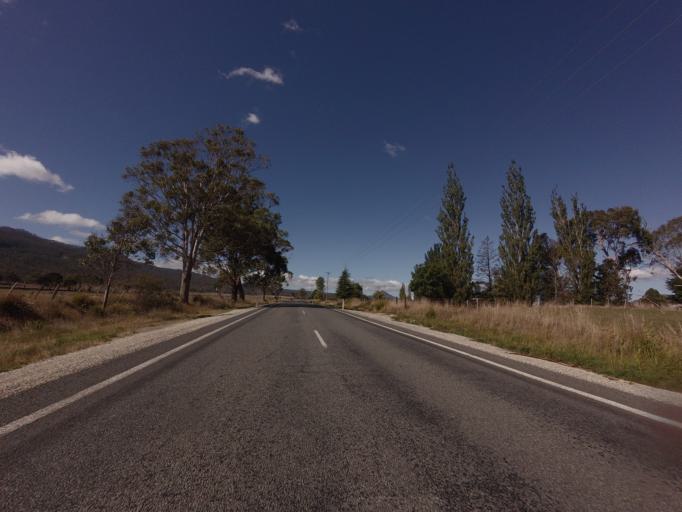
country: AU
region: Tasmania
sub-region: Break O'Day
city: St Helens
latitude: -41.5779
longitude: 148.1057
